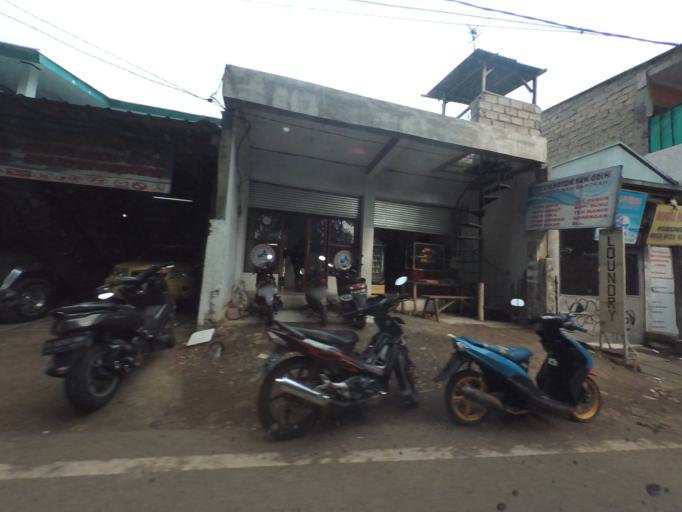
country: ID
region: West Java
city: Cicurug
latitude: -6.7562
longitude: 106.7992
